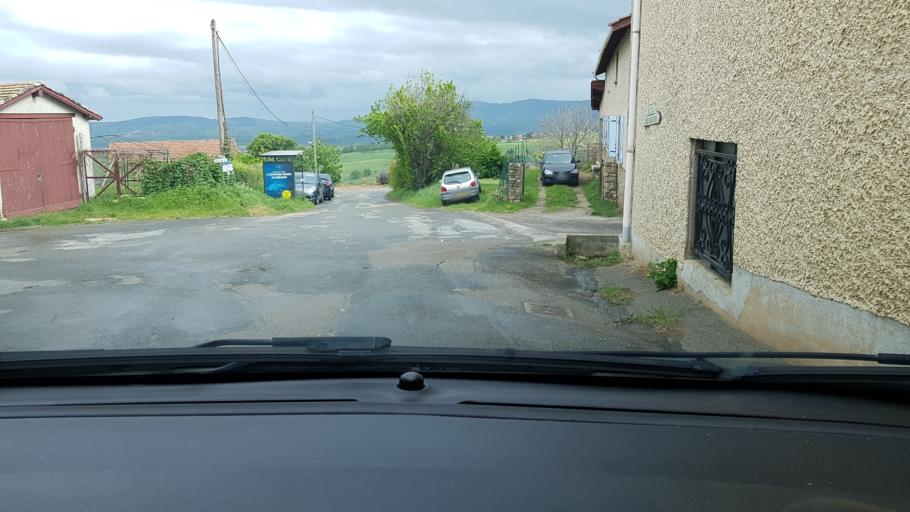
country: FR
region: Rhone-Alpes
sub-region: Departement du Rhone
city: Saint-Maurice-sur-Dargoire
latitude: 45.6030
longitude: 4.6299
